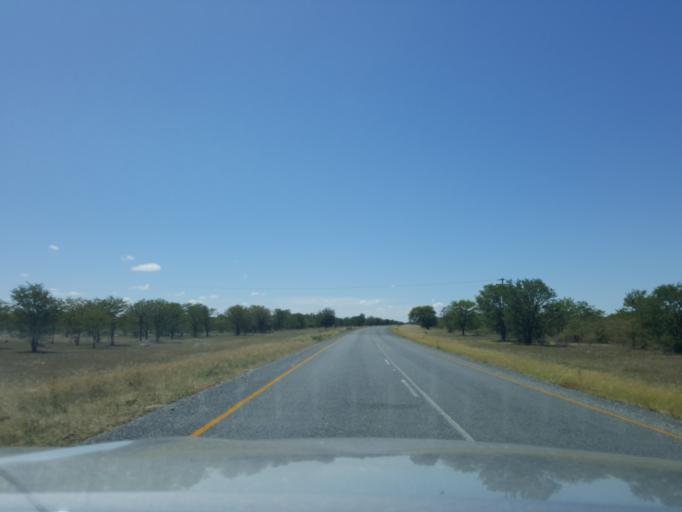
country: BW
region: Central
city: Gweta
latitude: -20.1893
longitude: 25.2387
